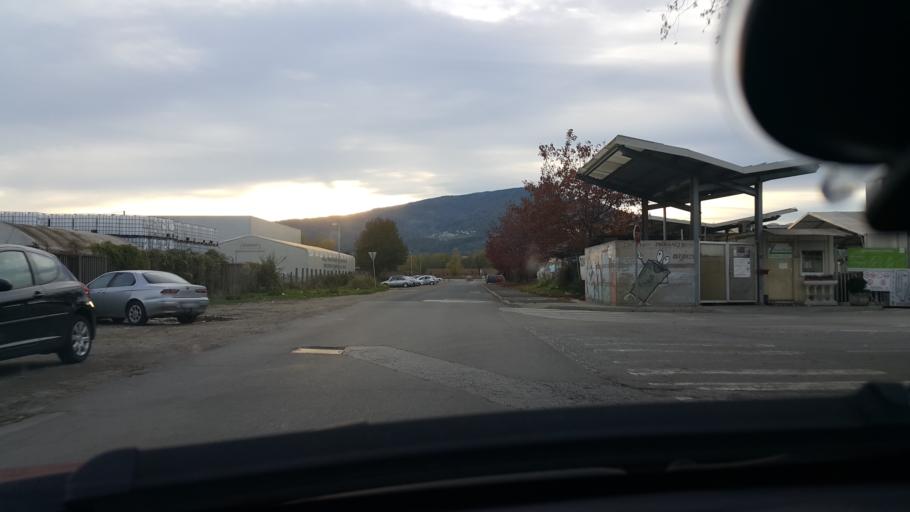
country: SI
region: Maribor
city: Razvanje
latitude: 46.5277
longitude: 15.6599
